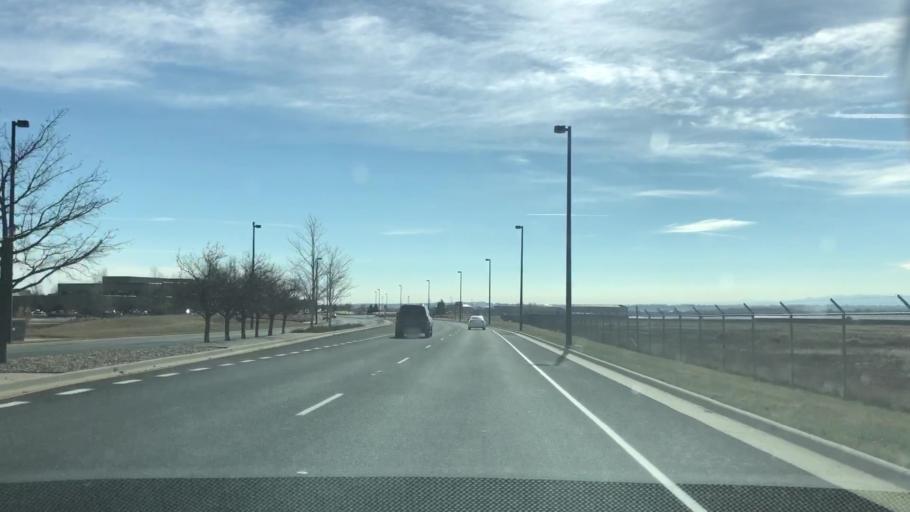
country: US
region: Colorado
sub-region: Larimer County
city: Loveland
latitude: 40.4341
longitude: -105.0071
